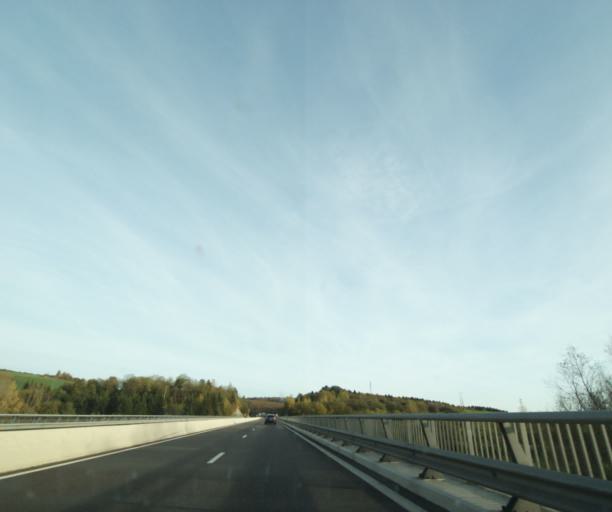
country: FR
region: Lorraine
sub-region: Departement de la Meuse
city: Dugny-sur-Meuse
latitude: 49.1112
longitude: 5.4091
